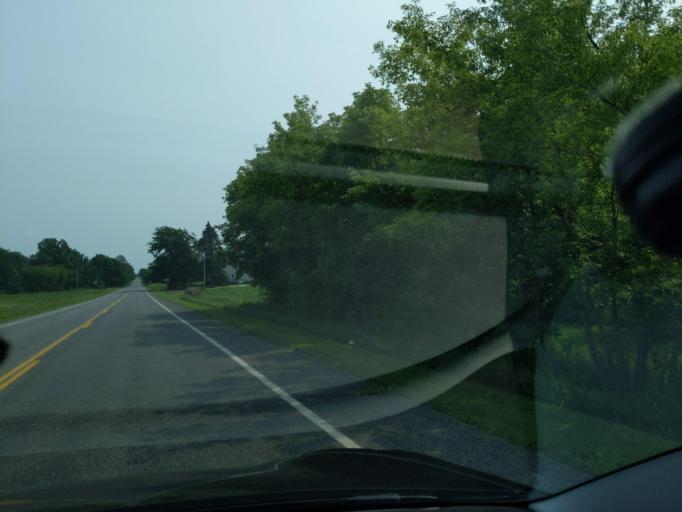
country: US
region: Michigan
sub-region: Eaton County
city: Eaton Rapids
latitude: 42.5352
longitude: -84.5620
